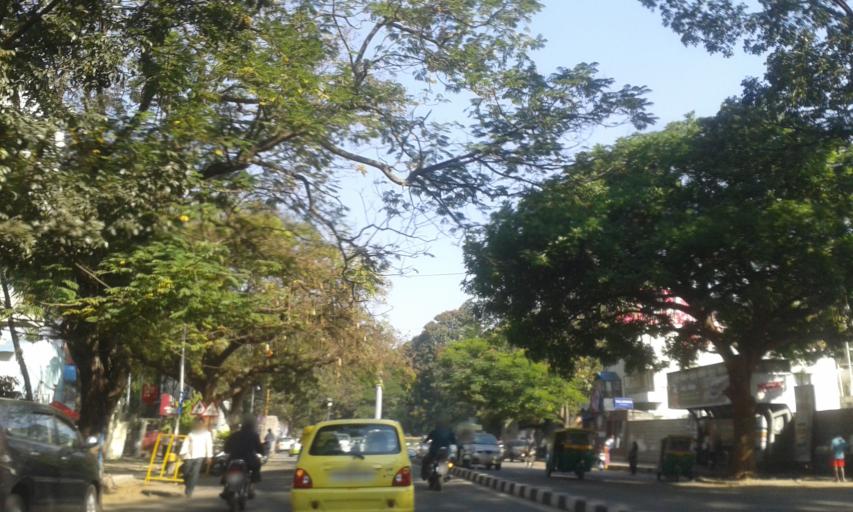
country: IN
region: Karnataka
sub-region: Bangalore Urban
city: Bangalore
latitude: 12.9428
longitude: 77.5852
